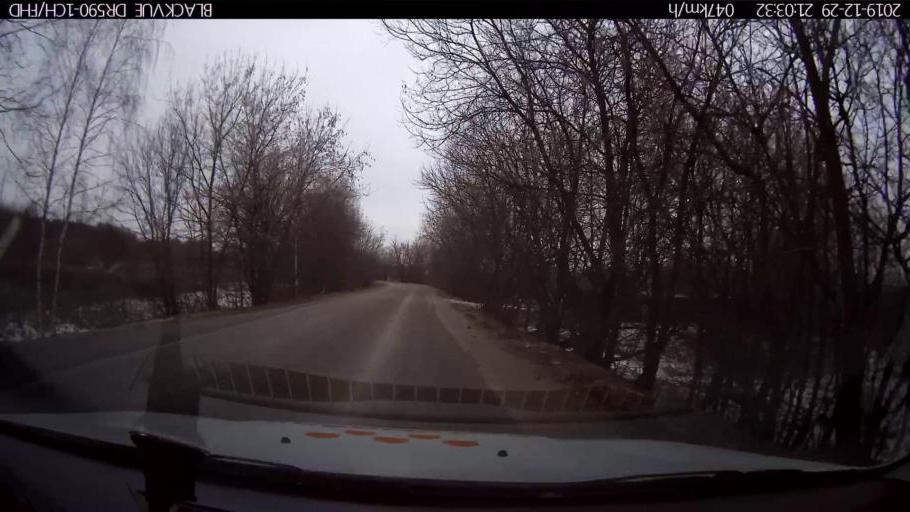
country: RU
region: Nizjnij Novgorod
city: Afonino
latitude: 56.1960
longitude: 44.0059
